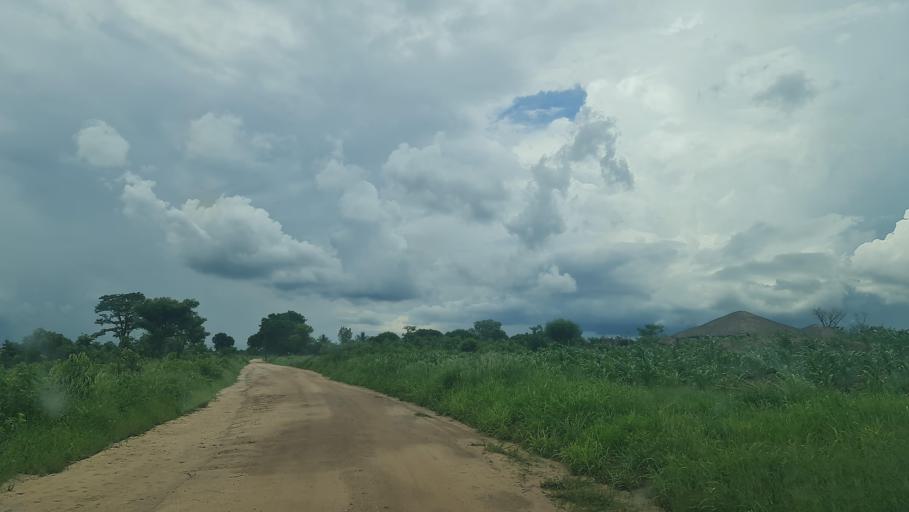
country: MW
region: Southern Region
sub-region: Nsanje District
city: Nsanje
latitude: -17.5777
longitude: 35.6597
